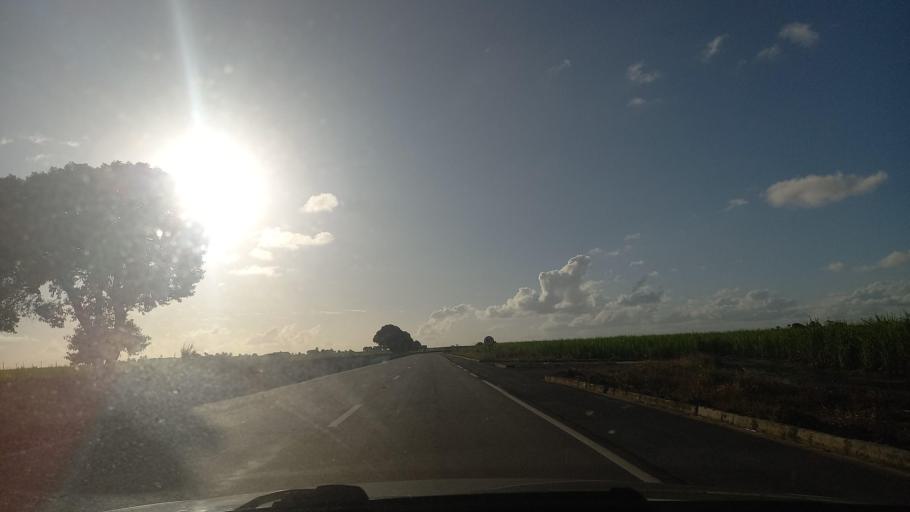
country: BR
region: Alagoas
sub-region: Campo Alegre
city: Campo Alegre
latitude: -9.8104
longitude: -36.2574
